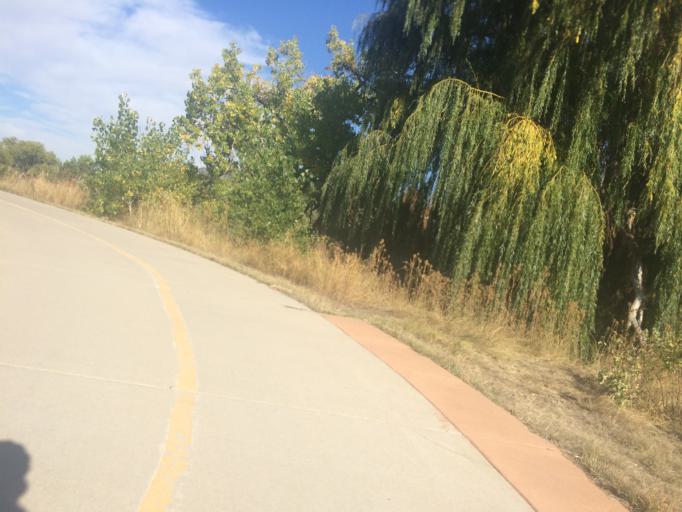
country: US
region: Colorado
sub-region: Broomfield County
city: Broomfield
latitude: 39.8750
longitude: -105.0812
